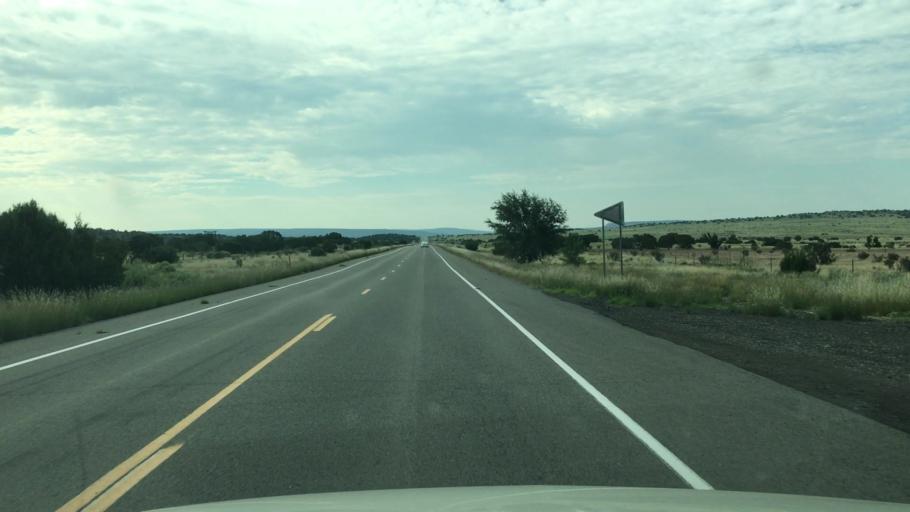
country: US
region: New Mexico
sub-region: Santa Fe County
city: Eldorado at Santa Fe
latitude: 35.4477
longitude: -105.8888
